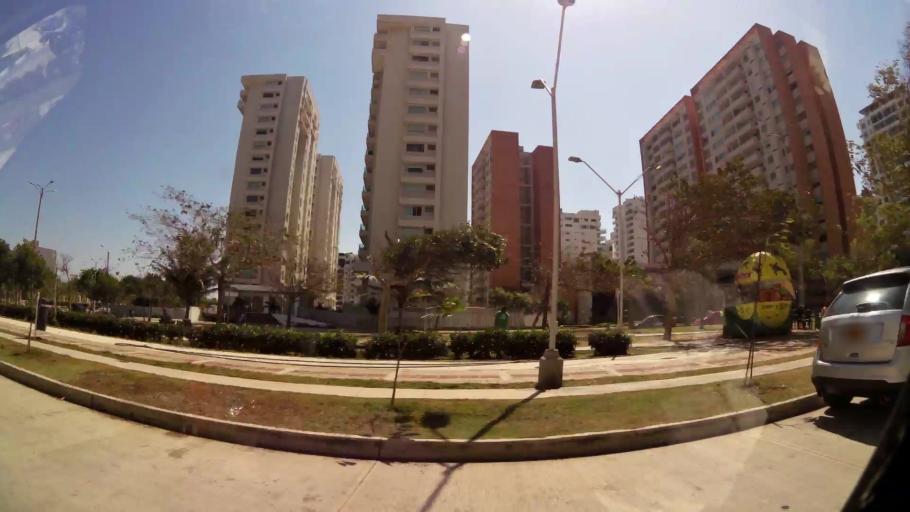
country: CO
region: Atlantico
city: Barranquilla
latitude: 11.0182
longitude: -74.8254
